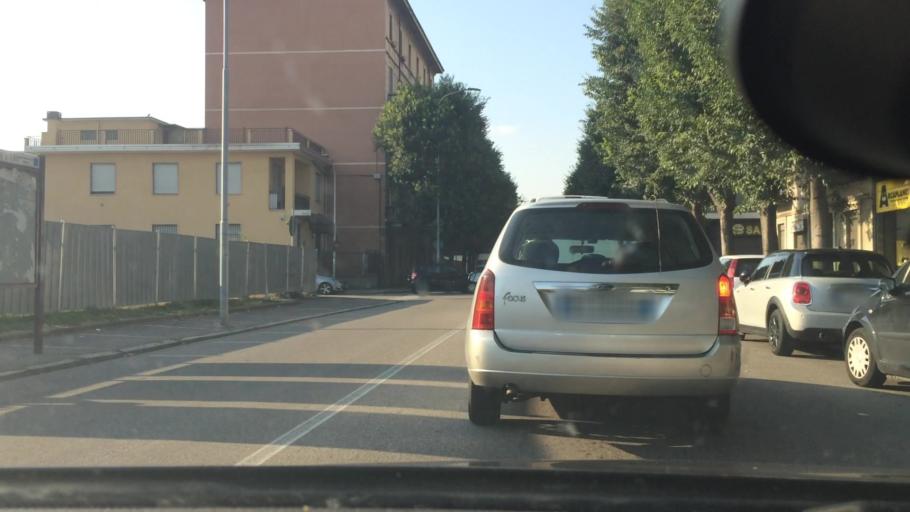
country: IT
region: Lombardy
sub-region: Citta metropolitana di Milano
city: Rho
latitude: 45.5274
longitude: 9.0465
